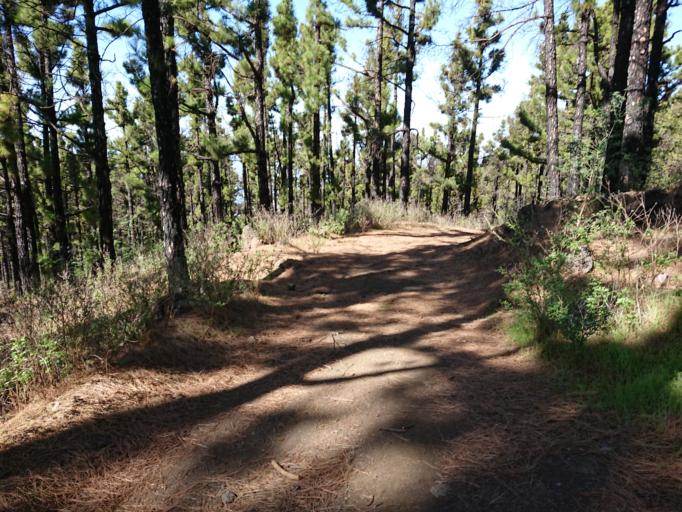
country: ES
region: Canary Islands
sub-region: Provincia de Santa Cruz de Tenerife
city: El Paso
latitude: 28.5932
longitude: -17.8613
